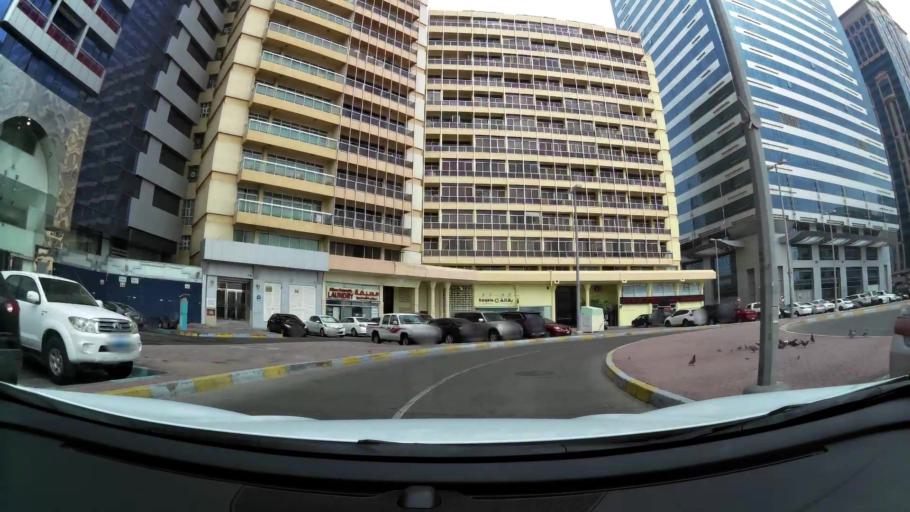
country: AE
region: Abu Dhabi
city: Abu Dhabi
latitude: 24.4825
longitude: 54.3604
